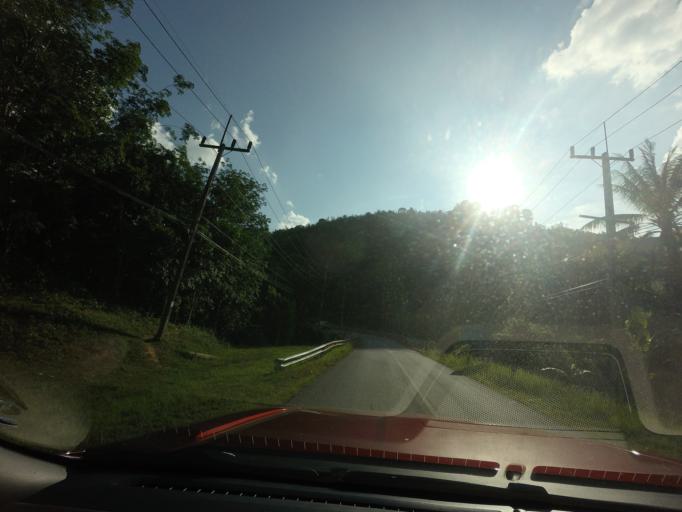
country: TH
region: Yala
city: Ban Nang Sata
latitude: 6.1953
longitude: 101.2508
